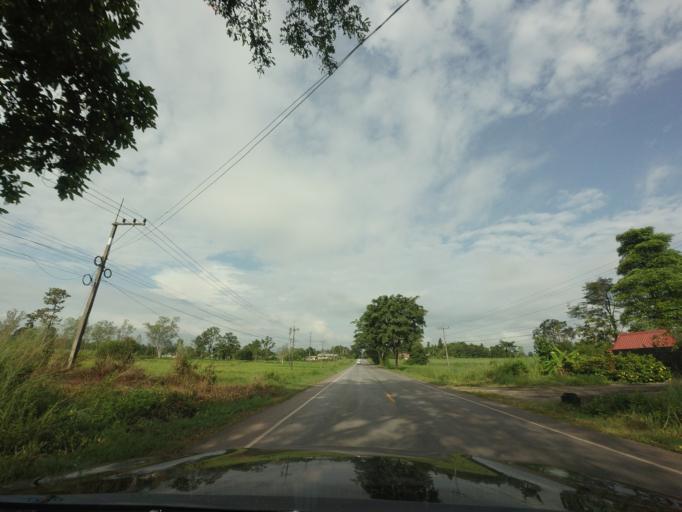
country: TH
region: Nong Khai
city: Pho Tak
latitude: 17.8039
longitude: 102.3059
